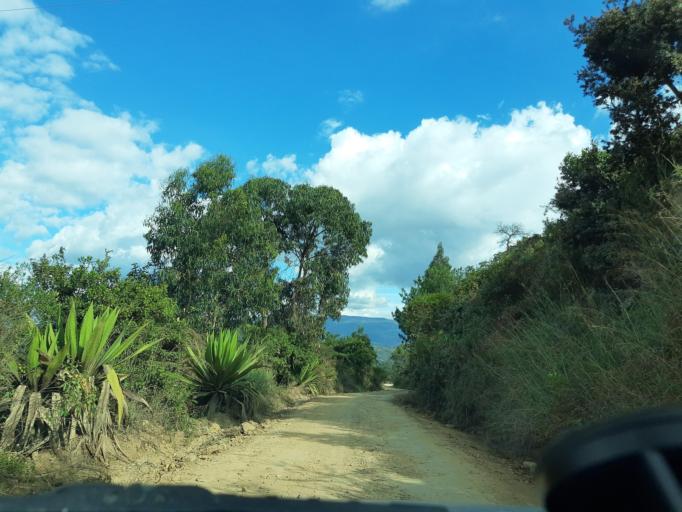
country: CO
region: Boyaca
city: Raquira
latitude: 5.5351
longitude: -73.6575
